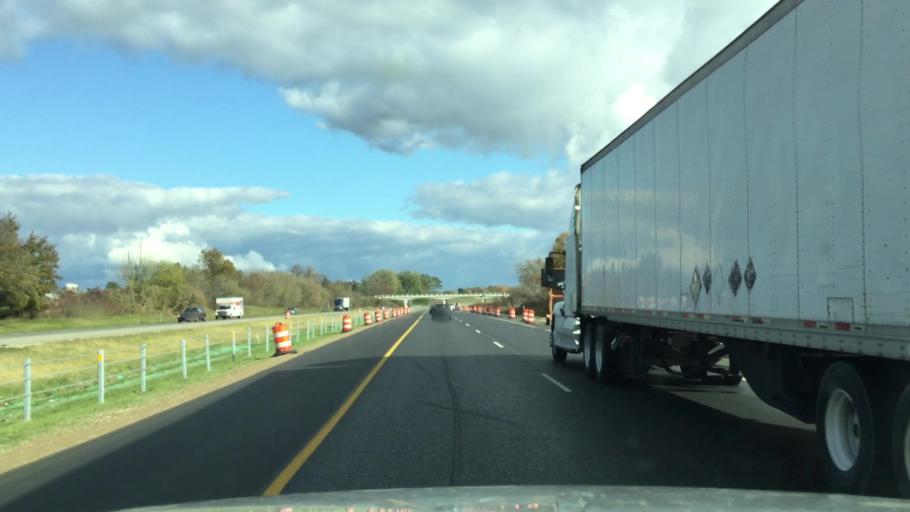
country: US
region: Michigan
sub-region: Van Buren County
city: Decatur
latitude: 42.1962
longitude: -86.0384
